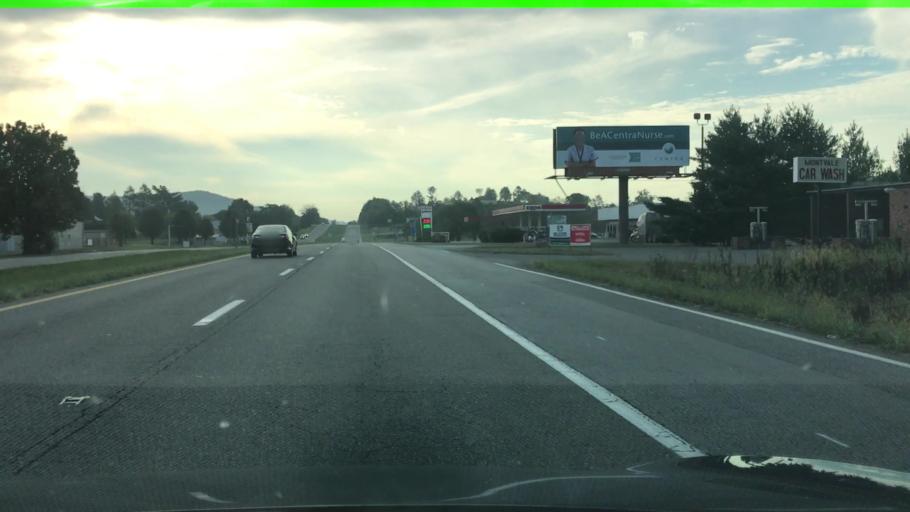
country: US
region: Virginia
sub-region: Botetourt County
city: Blue Ridge
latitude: 37.3833
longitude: -79.7292
